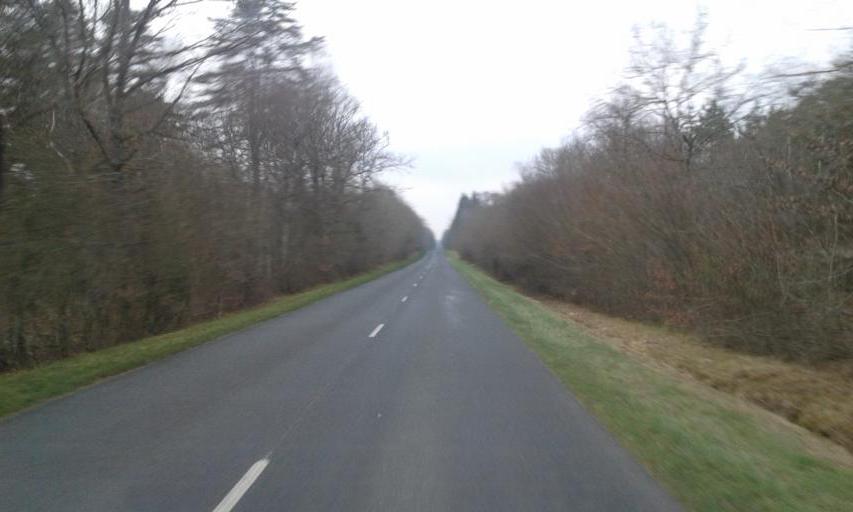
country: FR
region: Centre
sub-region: Departement du Loir-et-Cher
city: Dhuizon
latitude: 47.6273
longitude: 1.6630
